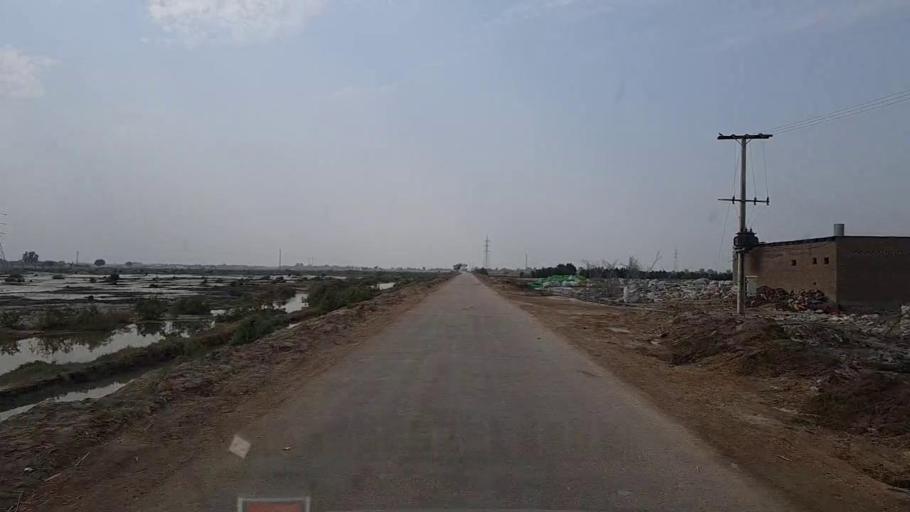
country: PK
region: Sindh
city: Mirwah Gorchani
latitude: 25.3371
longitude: 69.0490
